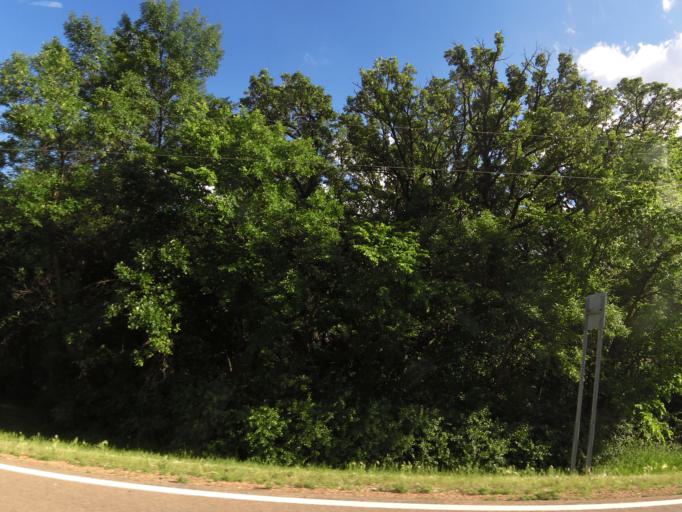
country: US
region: Minnesota
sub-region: Carver County
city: Victoria
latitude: 44.8115
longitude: -93.6774
